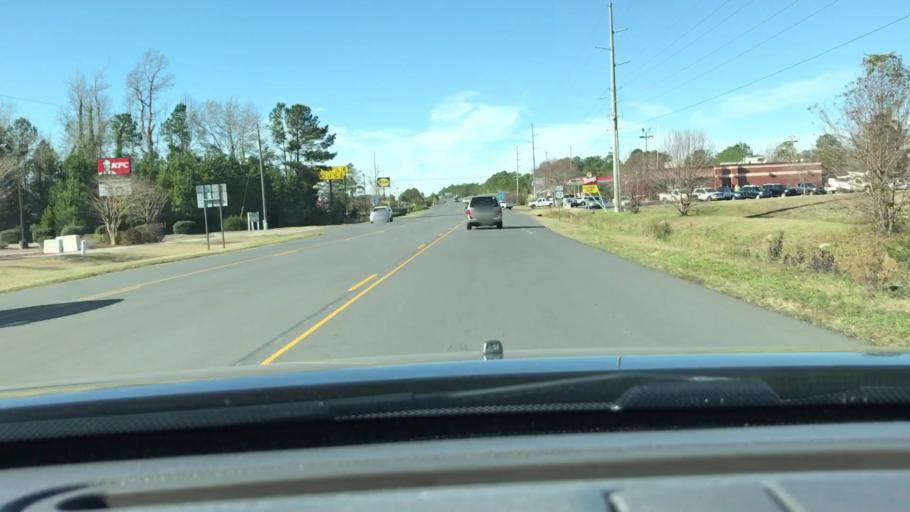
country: US
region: North Carolina
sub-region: Brunswick County
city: Shallotte
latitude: 33.9735
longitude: -78.4002
